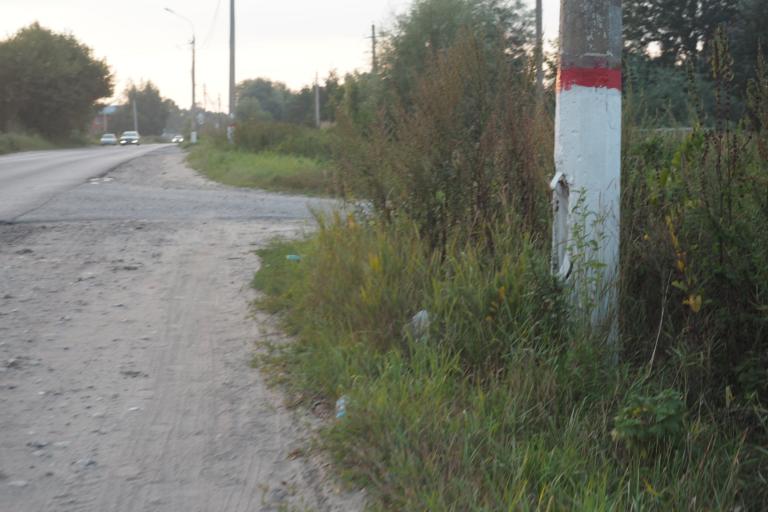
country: RU
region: Moskovskaya
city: Ramenskoye
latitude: 55.5823
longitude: 38.2629
